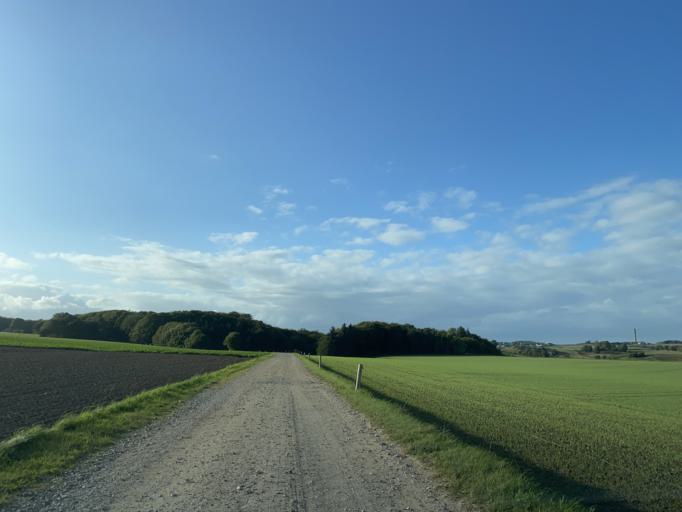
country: DK
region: Central Jutland
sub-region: Skanderborg Kommune
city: Ry
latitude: 56.1582
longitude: 9.8040
